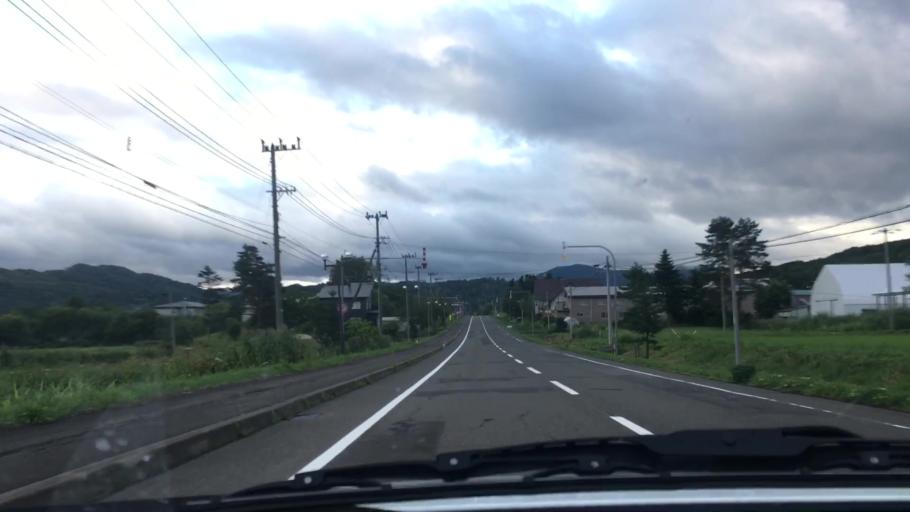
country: JP
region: Hokkaido
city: Shimo-furano
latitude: 42.9952
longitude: 142.4027
